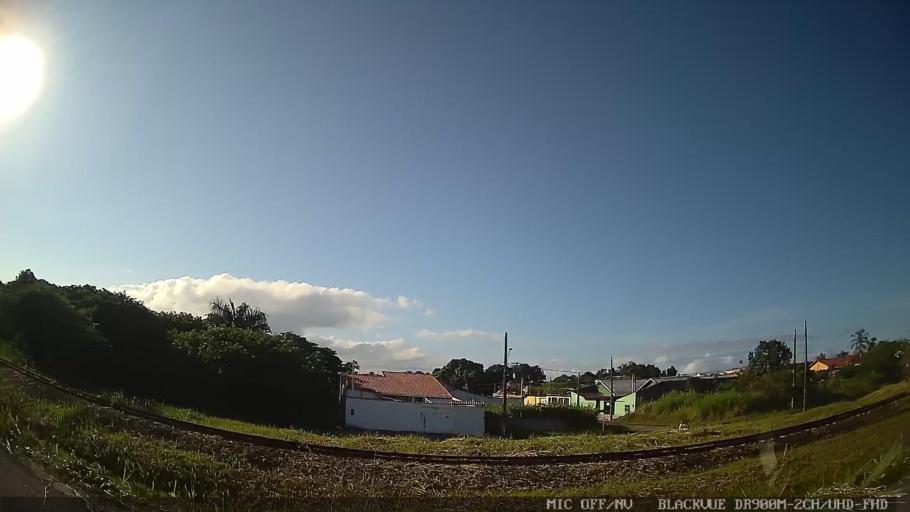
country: BR
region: Sao Paulo
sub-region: Peruibe
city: Peruibe
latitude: -24.2816
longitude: -46.9610
